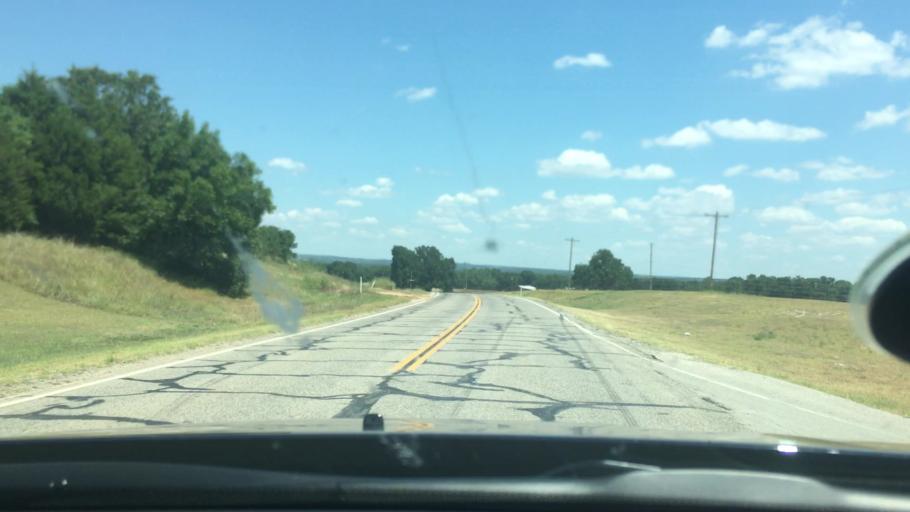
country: US
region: Oklahoma
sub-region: Carter County
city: Dickson
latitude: 34.2041
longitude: -96.9775
